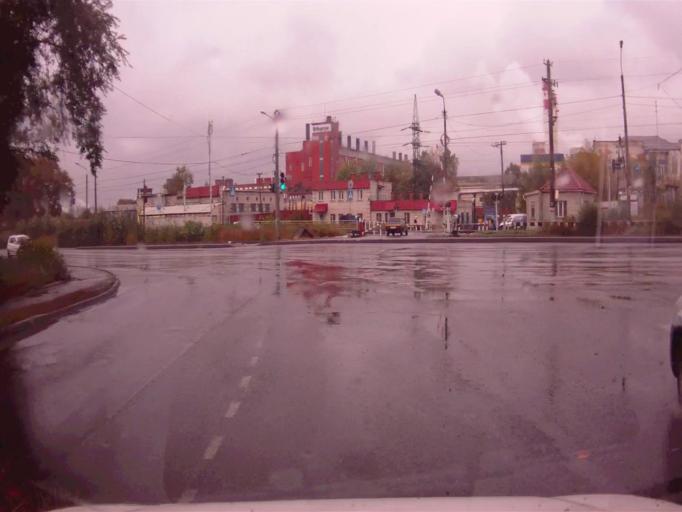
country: RU
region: Chelyabinsk
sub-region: Gorod Chelyabinsk
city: Chelyabinsk
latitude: 55.1984
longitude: 61.4067
